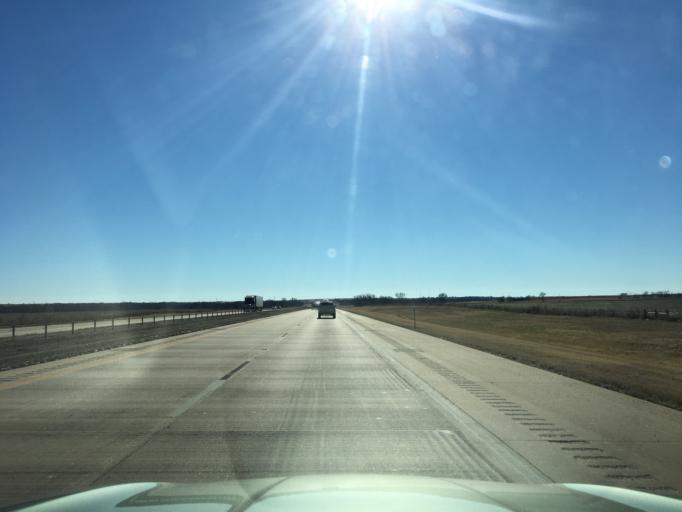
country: US
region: Oklahoma
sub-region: Noble County
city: Perry
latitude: 36.4481
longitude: -97.3271
